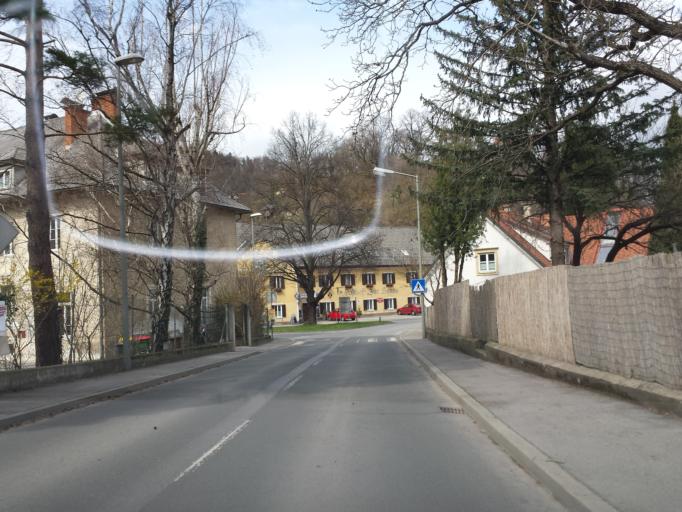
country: AT
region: Styria
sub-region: Graz Stadt
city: Goesting
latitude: 47.0989
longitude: 15.3930
